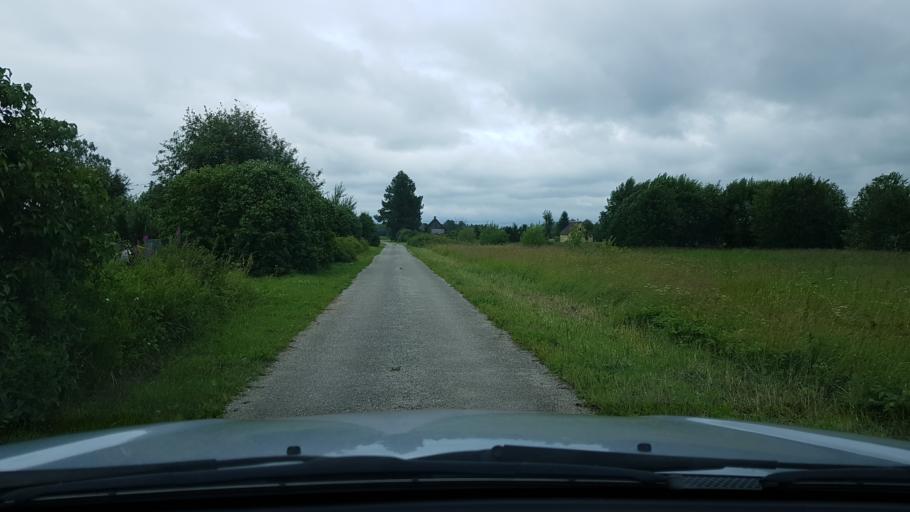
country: EE
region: Ida-Virumaa
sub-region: Narva-Joesuu linn
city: Narva-Joesuu
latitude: 59.3436
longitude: 27.9447
